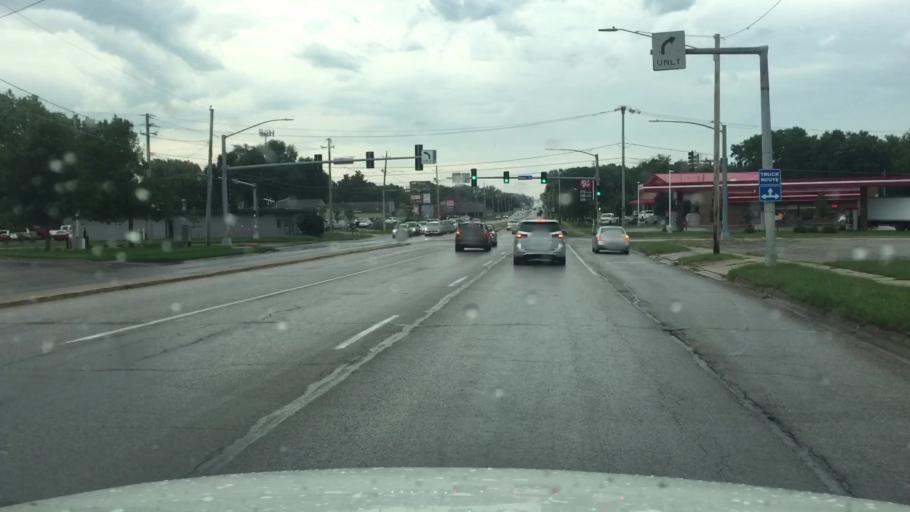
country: US
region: Iowa
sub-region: Polk County
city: Des Moines
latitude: 41.5820
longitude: -93.5970
